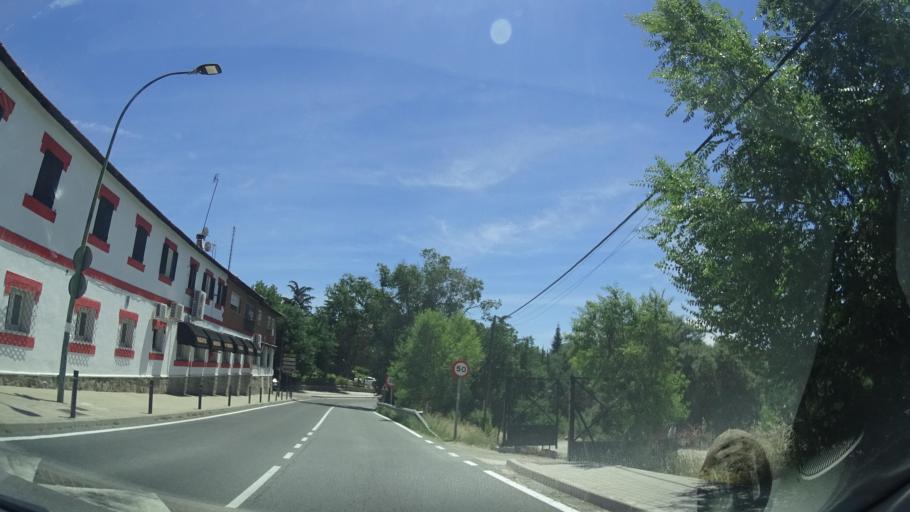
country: ES
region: Madrid
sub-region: Provincia de Madrid
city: Galapagar
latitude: 40.6004
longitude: -3.9831
